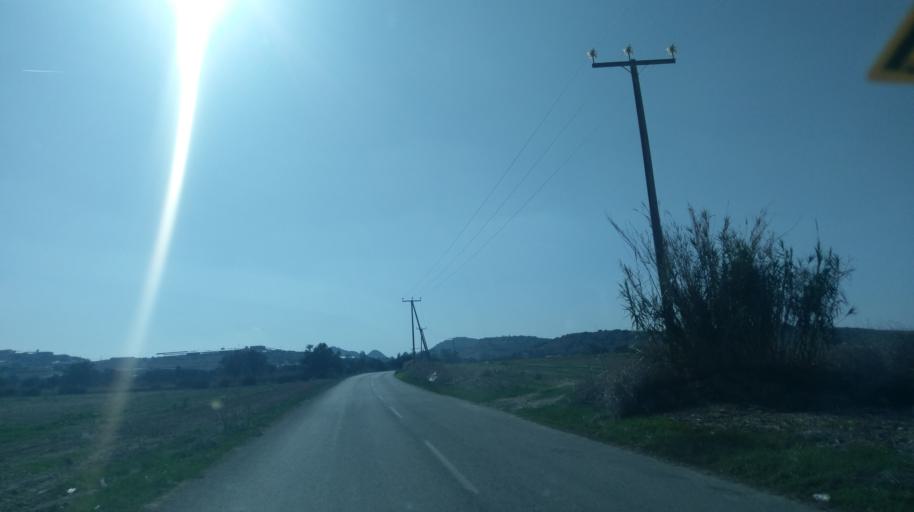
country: CY
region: Lefkosia
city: Lympia
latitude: 35.0264
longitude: 33.4715
